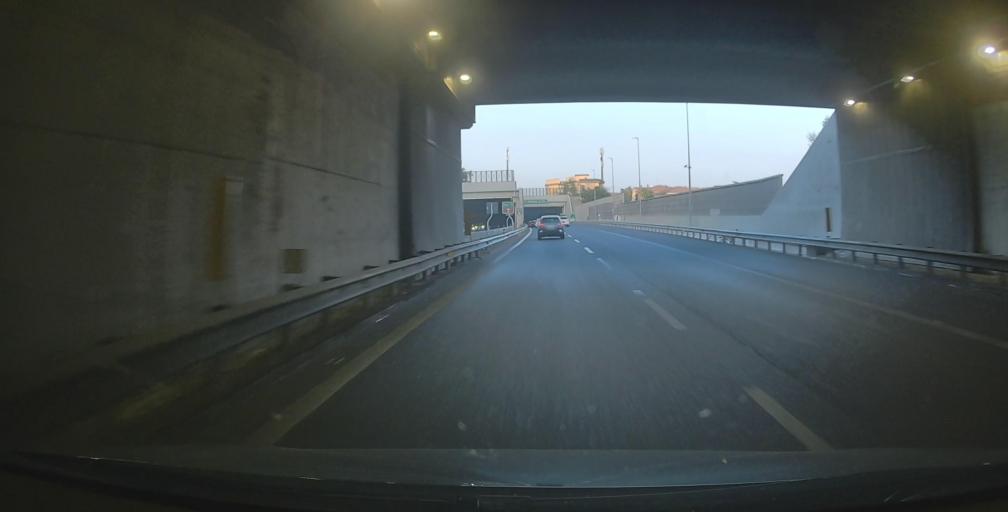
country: IT
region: Sicily
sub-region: Catania
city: Sant'Agata Li Battiati
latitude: 37.5502
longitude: 15.0765
